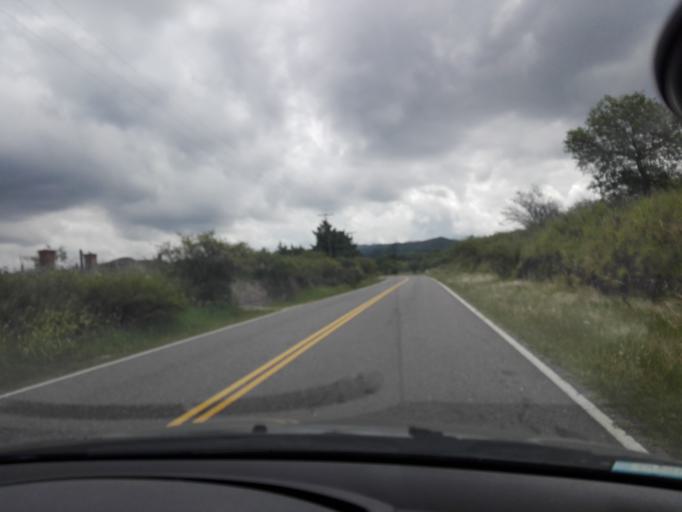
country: AR
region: Cordoba
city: Alta Gracia
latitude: -31.5928
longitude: -64.4838
